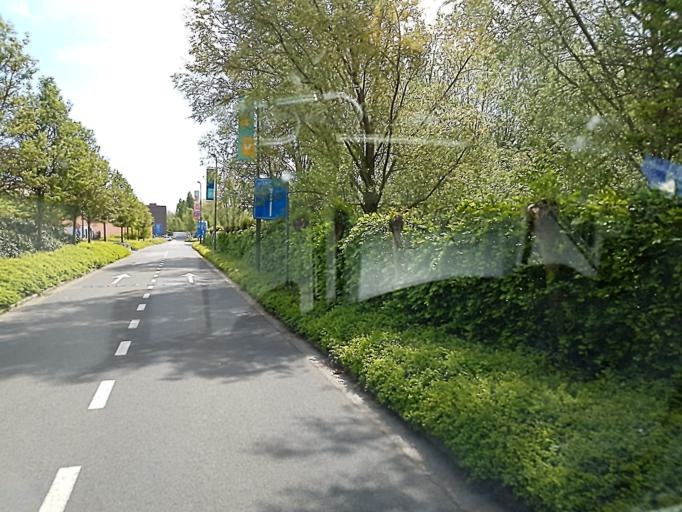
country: BE
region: Flanders
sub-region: Provincie Oost-Vlaanderen
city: Sint-Niklaas
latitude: 51.1535
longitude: 4.1510
